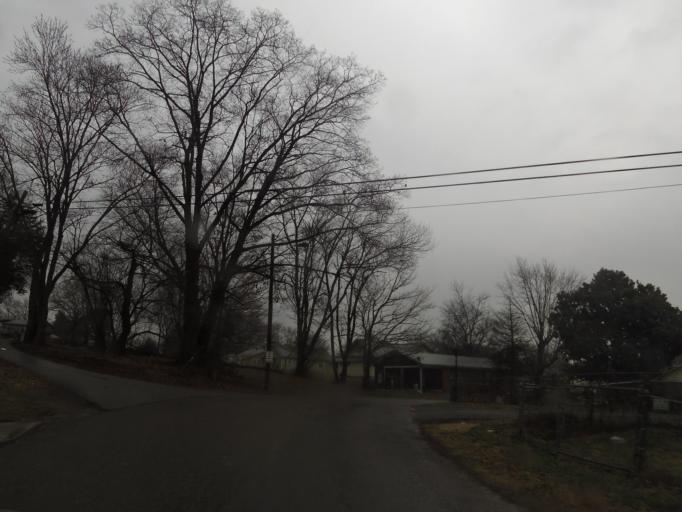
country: US
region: Tennessee
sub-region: Knox County
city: Knoxville
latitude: 35.9733
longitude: -83.9528
